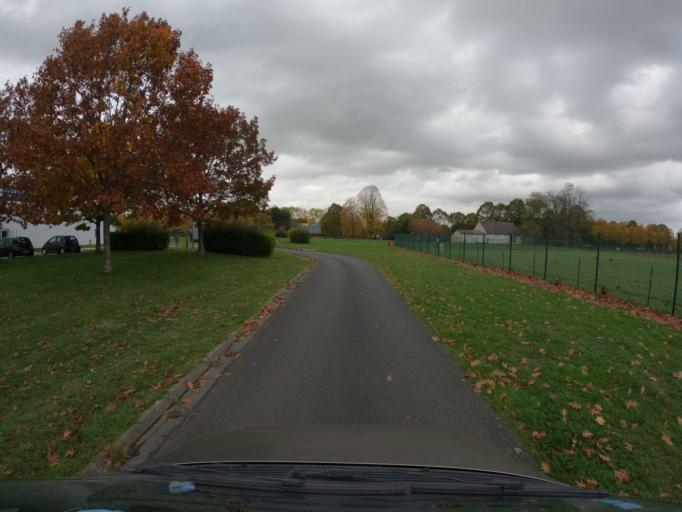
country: FR
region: Ile-de-France
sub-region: Departement de Seine-et-Marne
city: Lognes
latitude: 48.8239
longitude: 2.6292
